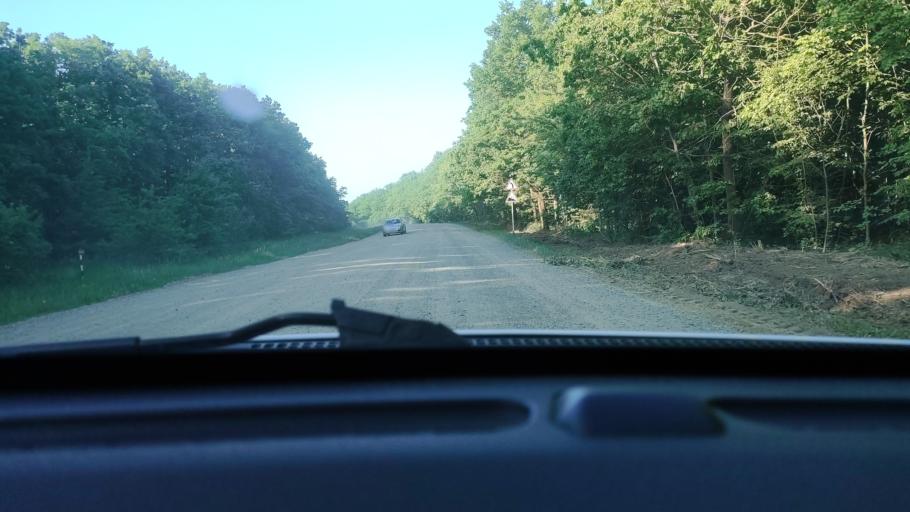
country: RU
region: Krasnodarskiy
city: Goryachiy Klyuch
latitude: 44.7059
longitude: 38.9906
